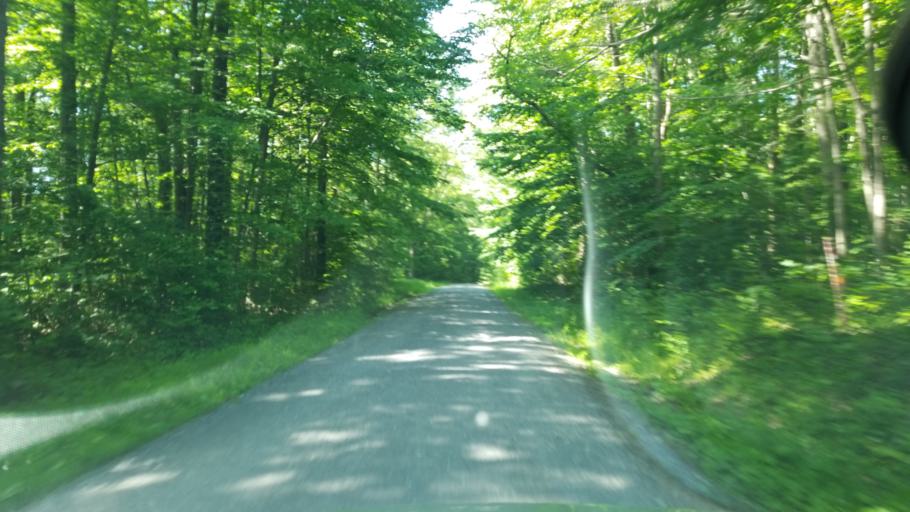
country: US
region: Pennsylvania
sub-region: Clearfield County
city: Clearfield
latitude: 41.2001
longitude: -78.4834
